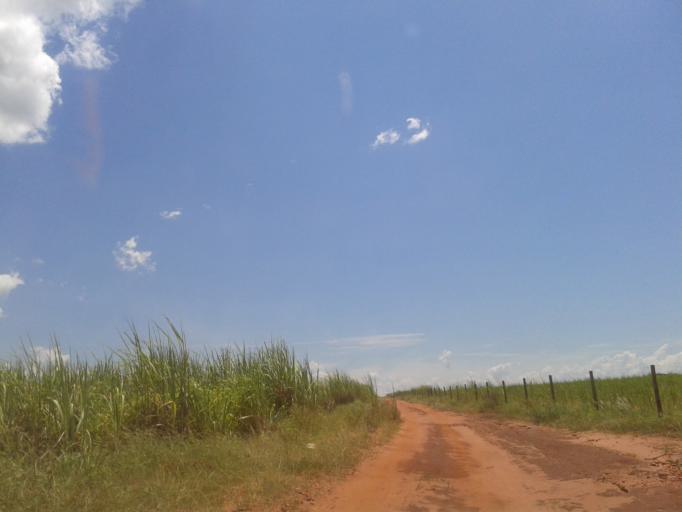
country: BR
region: Minas Gerais
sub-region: Santa Vitoria
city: Santa Vitoria
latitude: -19.1628
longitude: -50.4165
